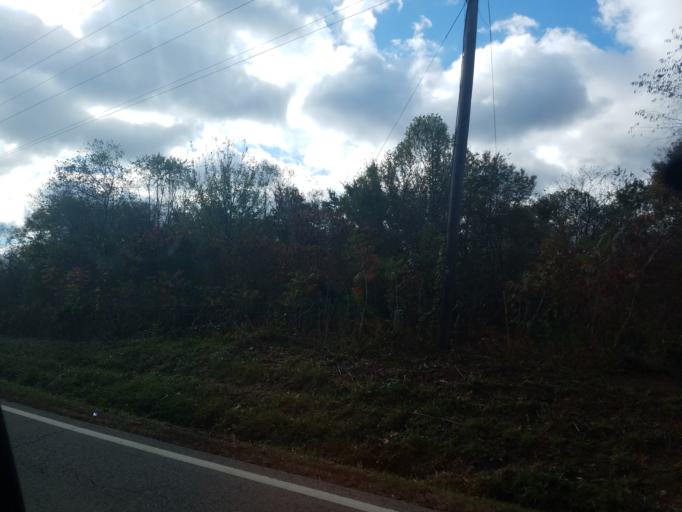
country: US
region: Ohio
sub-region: Vinton County
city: McArthur
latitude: 39.1909
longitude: -82.4732
